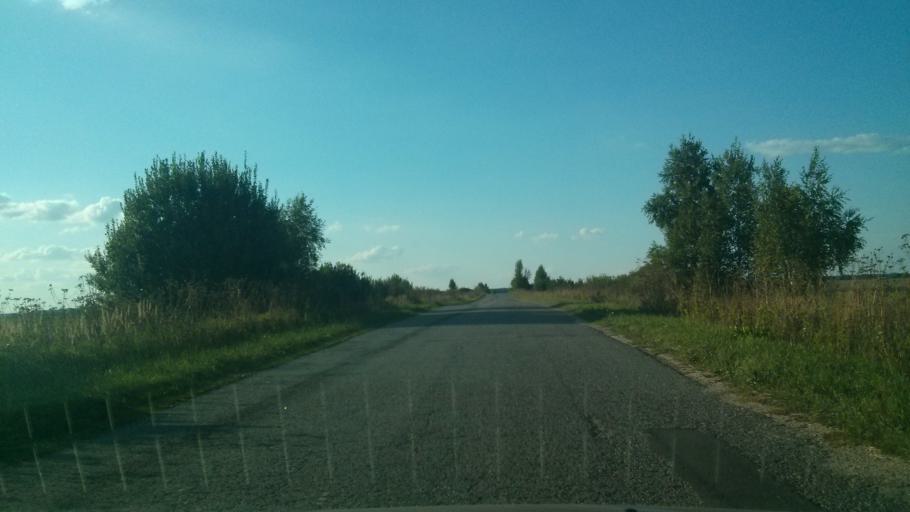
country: RU
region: Vladimir
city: Melenki
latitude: 55.2985
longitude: 41.7933
